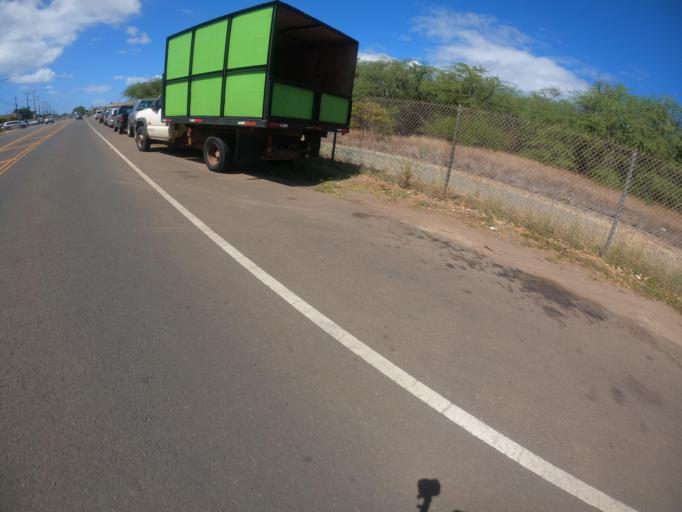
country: US
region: Hawaii
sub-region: Honolulu County
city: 'Ewa Beach
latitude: 21.3129
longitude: -158.0024
